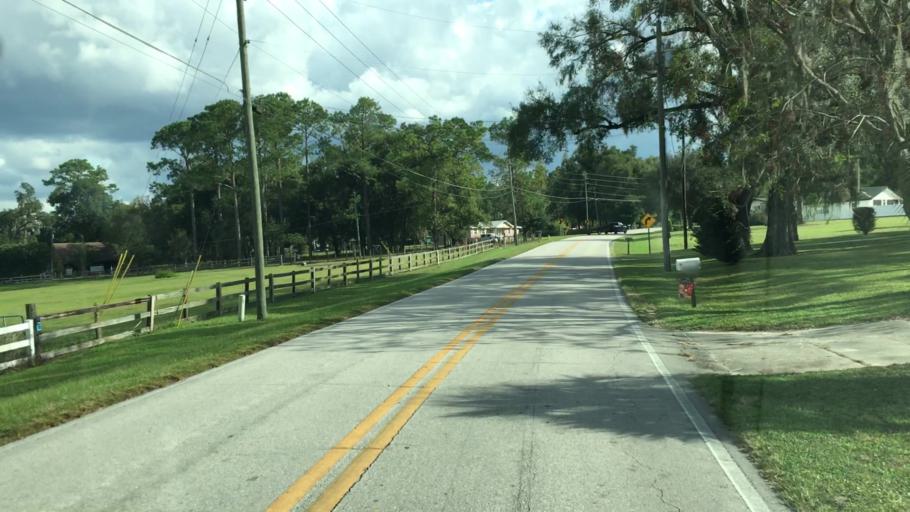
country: US
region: Florida
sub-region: Volusia County
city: North DeLand
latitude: 29.0748
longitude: -81.2723
